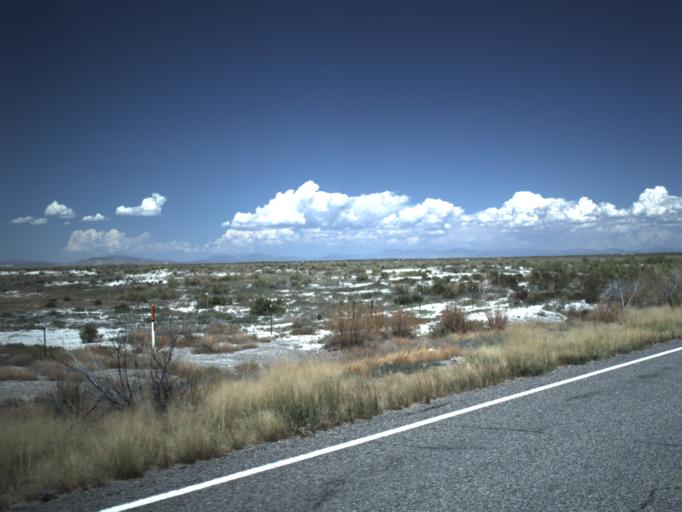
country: US
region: Utah
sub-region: Millard County
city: Delta
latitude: 39.2723
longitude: -112.8597
